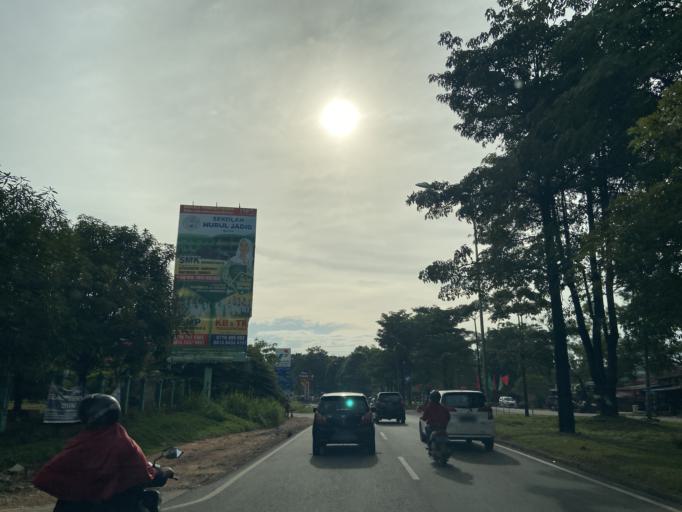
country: SG
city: Singapore
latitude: 1.1327
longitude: 104.0208
